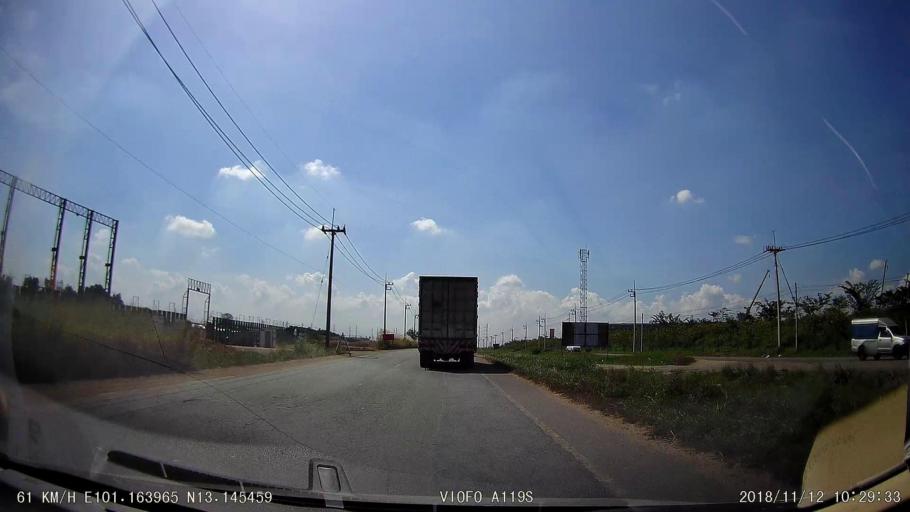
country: TH
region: Rayong
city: Pluak Daeng
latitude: 13.1365
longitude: 101.1675
